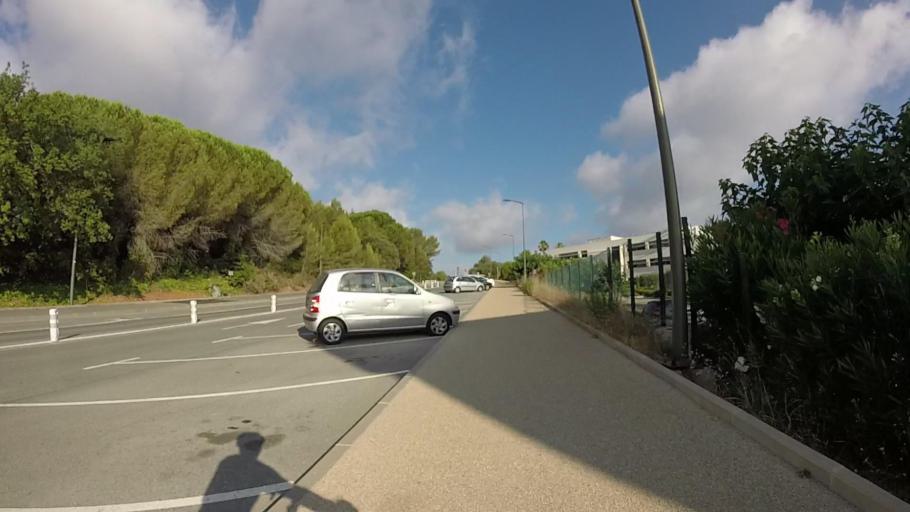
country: FR
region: Provence-Alpes-Cote d'Azur
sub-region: Departement des Alpes-Maritimes
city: Biot
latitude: 43.6234
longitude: 7.0613
